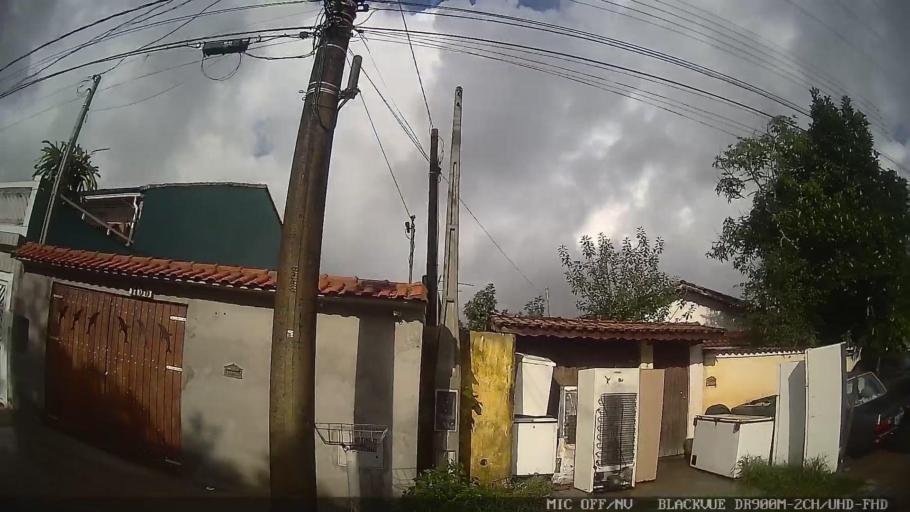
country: BR
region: Sao Paulo
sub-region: Itanhaem
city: Itanhaem
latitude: -24.2236
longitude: -46.8890
